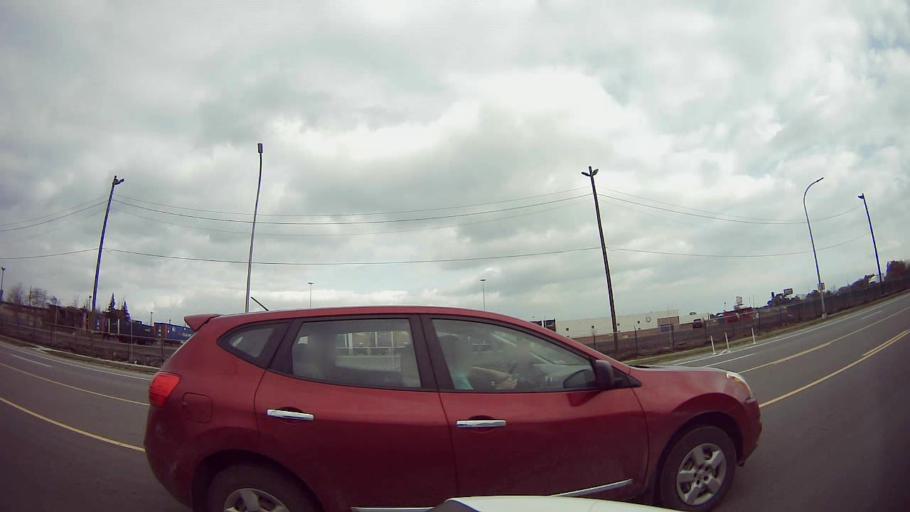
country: US
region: Michigan
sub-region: Wayne County
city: Dearborn
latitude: 42.3399
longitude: -83.1268
